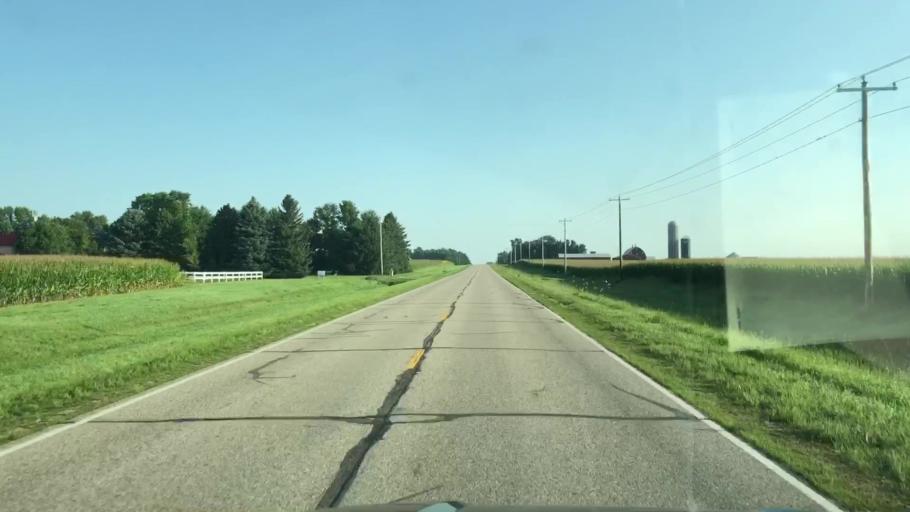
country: US
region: Iowa
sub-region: Lyon County
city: George
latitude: 43.3681
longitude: -95.9983
